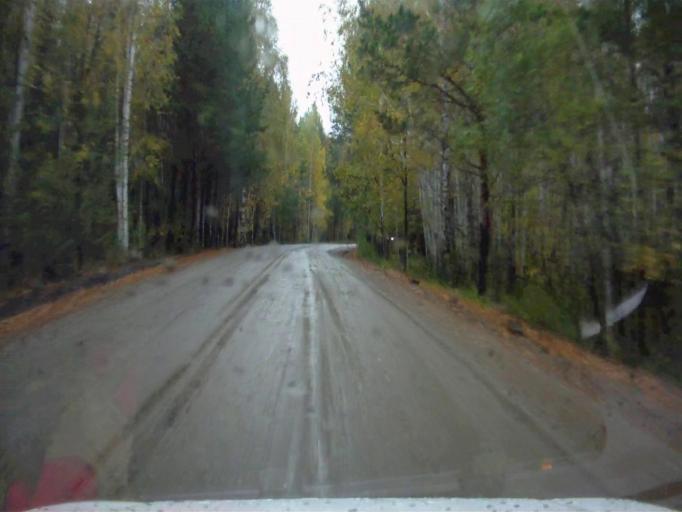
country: RU
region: Chelyabinsk
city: Kyshtym
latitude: 55.7490
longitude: 60.4885
